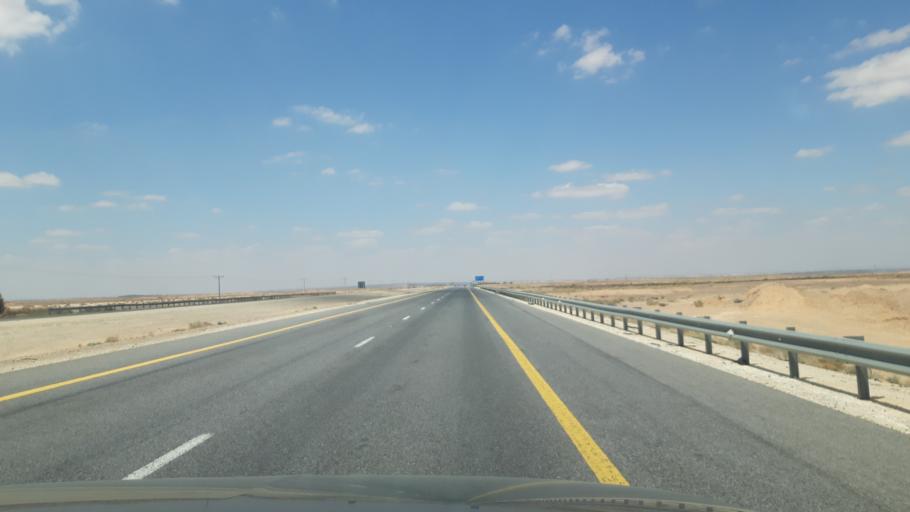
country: JO
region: Amman
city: Al Azraq ash Shamali
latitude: 31.7181
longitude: 36.8478
